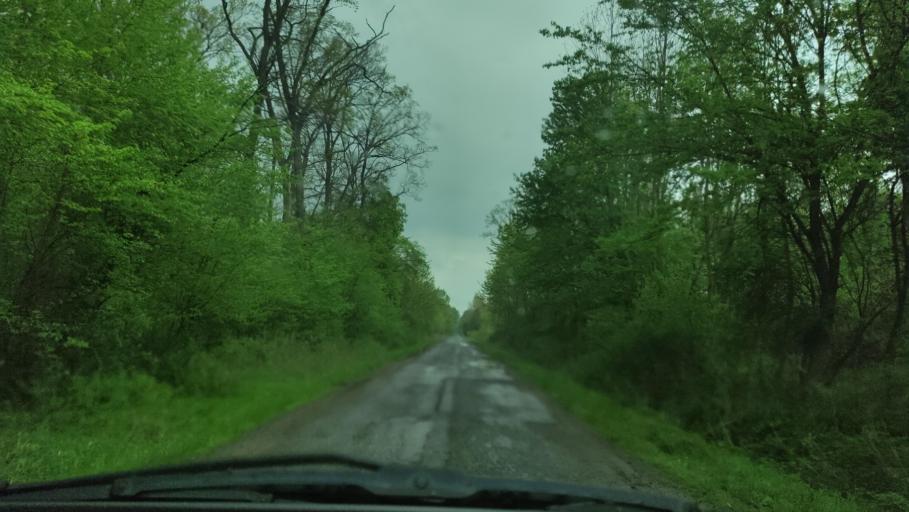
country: HU
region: Baranya
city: Mohacs
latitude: 45.9156
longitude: 18.7298
